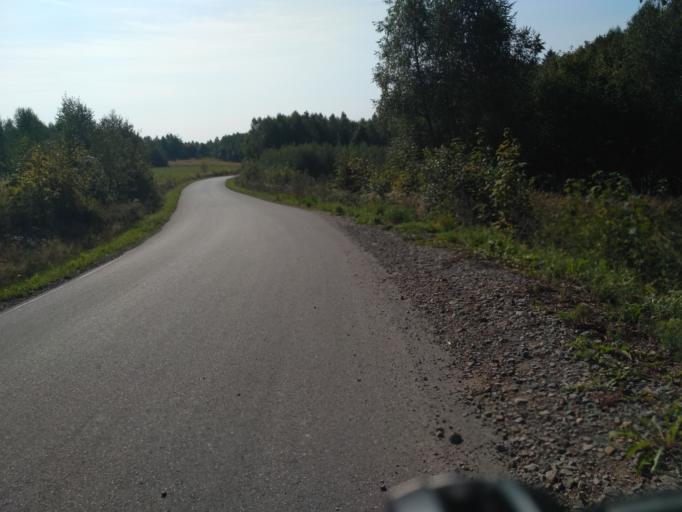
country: PL
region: Subcarpathian Voivodeship
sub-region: Powiat strzyzowski
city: Gwoznica Gorna
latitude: 49.8064
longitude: 22.0233
